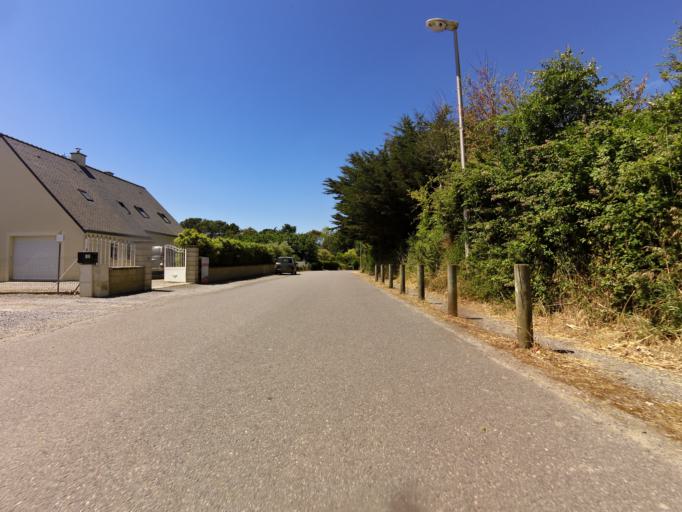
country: FR
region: Brittany
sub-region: Departement du Morbihan
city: Penestin
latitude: 47.4664
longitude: -2.4835
